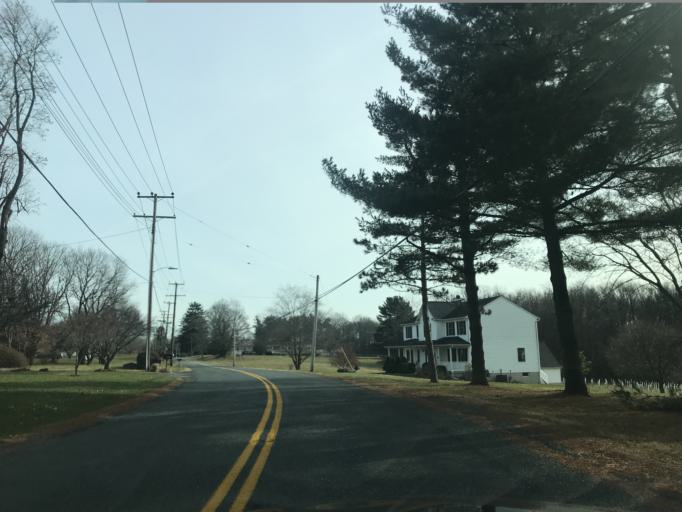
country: US
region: Maryland
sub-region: Harford County
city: Aberdeen
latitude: 39.5724
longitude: -76.1637
